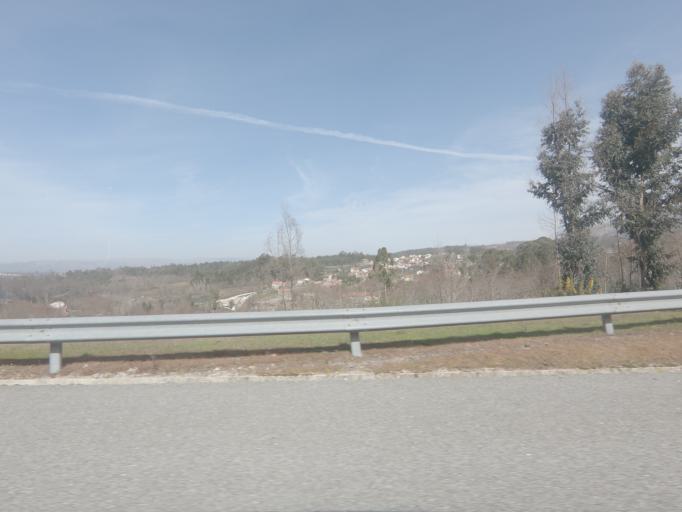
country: PT
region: Viseu
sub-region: Oliveira de Frades
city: Oliveira de Frades
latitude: 40.6809
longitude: -8.1701
